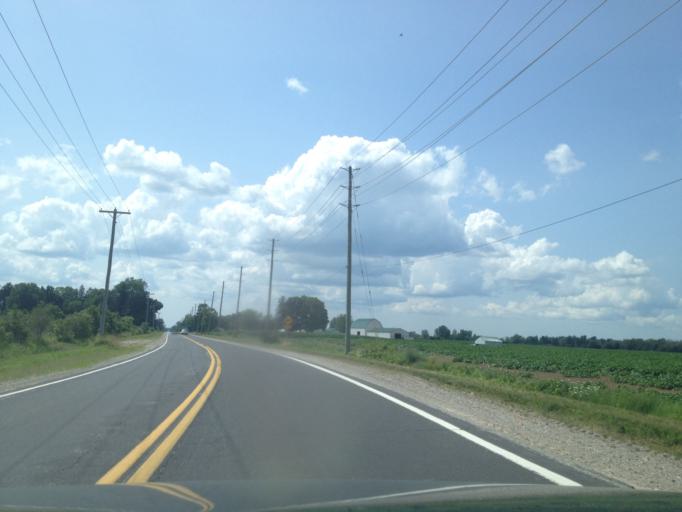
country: CA
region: Ontario
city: Aylmer
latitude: 42.6620
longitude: -80.8124
